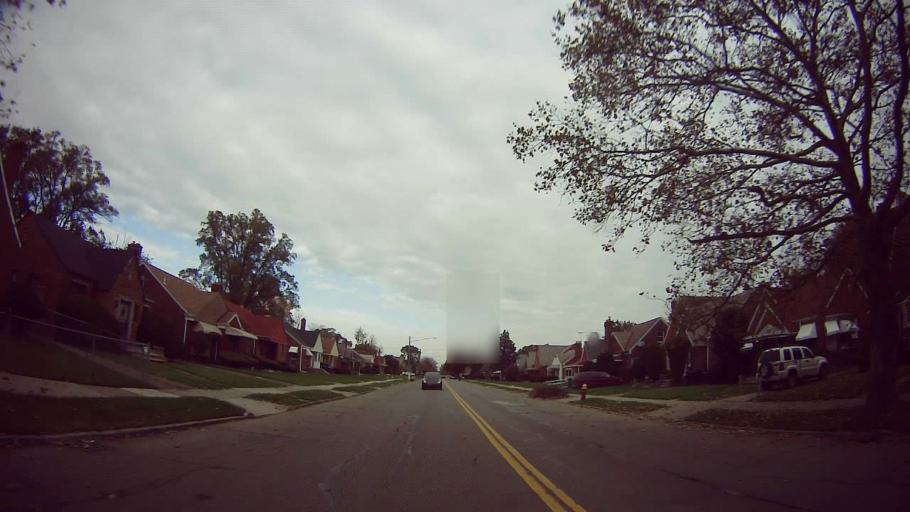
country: US
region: Michigan
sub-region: Wayne County
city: Dearborn
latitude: 42.3667
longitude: -83.1876
